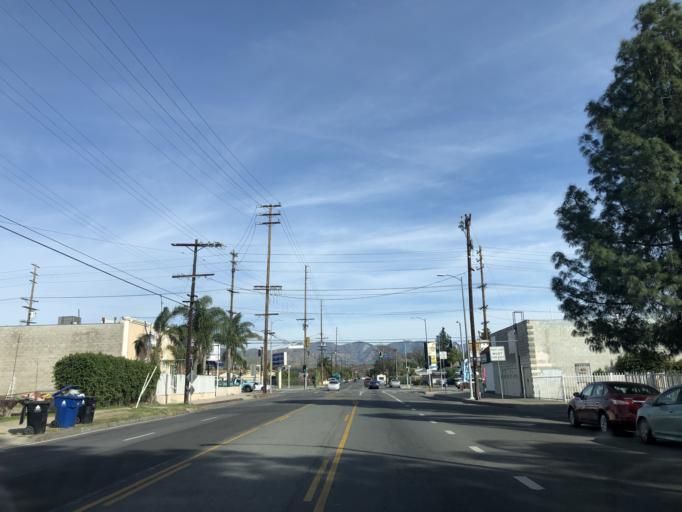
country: US
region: California
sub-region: Los Angeles County
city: San Fernando
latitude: 34.2522
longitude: -118.4266
